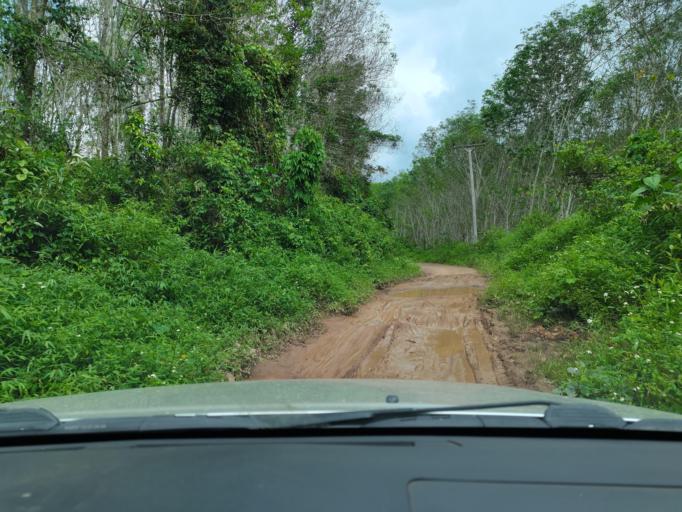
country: LA
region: Loungnamtha
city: Muang Long
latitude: 20.7009
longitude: 101.0298
